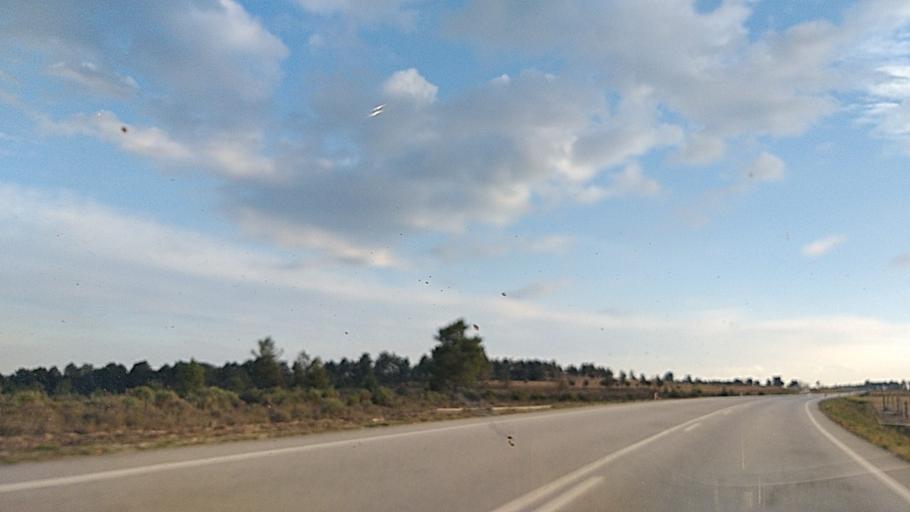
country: PT
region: Guarda
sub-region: Pinhel
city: Pinhel
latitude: 40.6555
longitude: -6.9665
